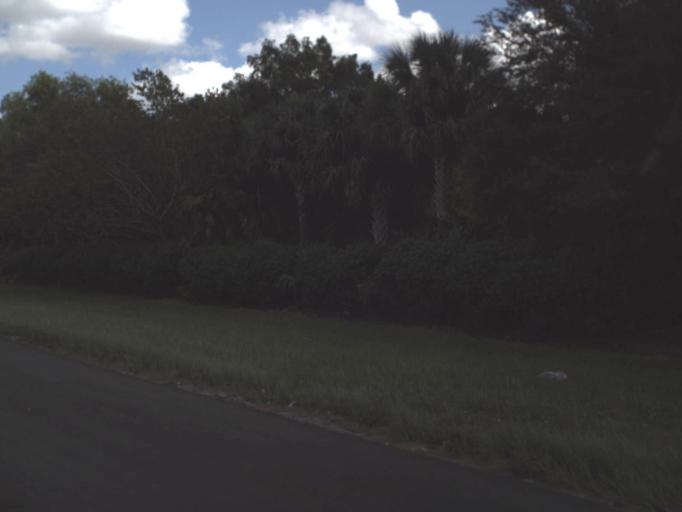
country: US
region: Florida
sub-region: Broward County
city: Tamarac
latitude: 26.1800
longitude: -80.3063
